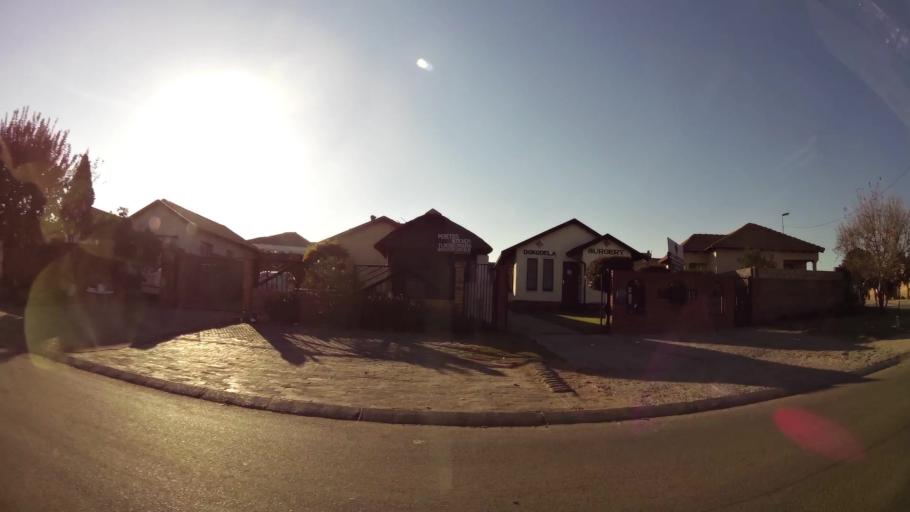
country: ZA
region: Gauteng
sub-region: City of Johannesburg Metropolitan Municipality
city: Modderfontein
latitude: -26.0484
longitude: 28.1595
